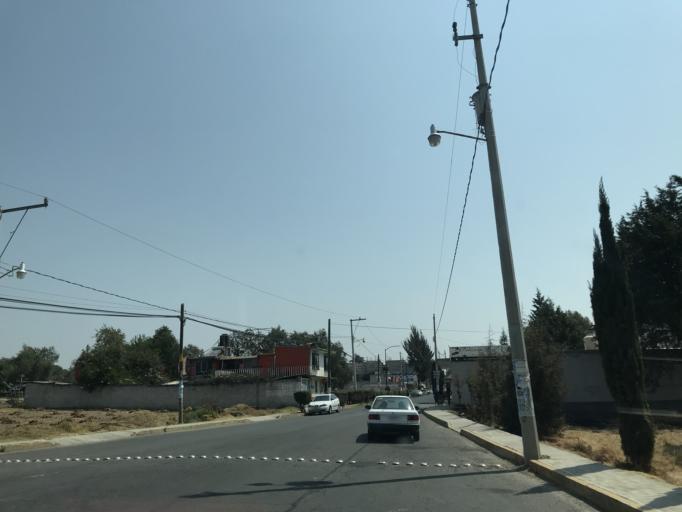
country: MX
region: Tlaxcala
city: Yauhquemehcan
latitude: 19.4030
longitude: -98.1861
